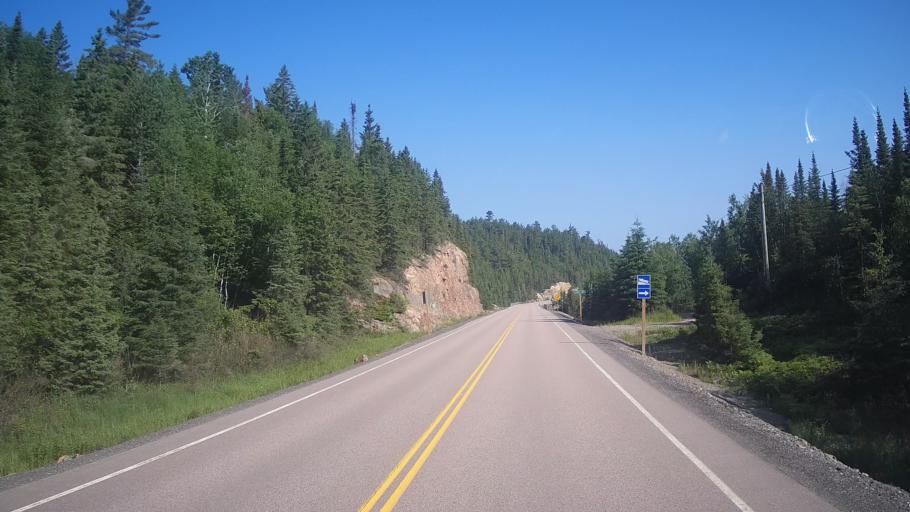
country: CA
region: Ontario
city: Rayside-Balfour
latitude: 47.0155
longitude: -81.6359
